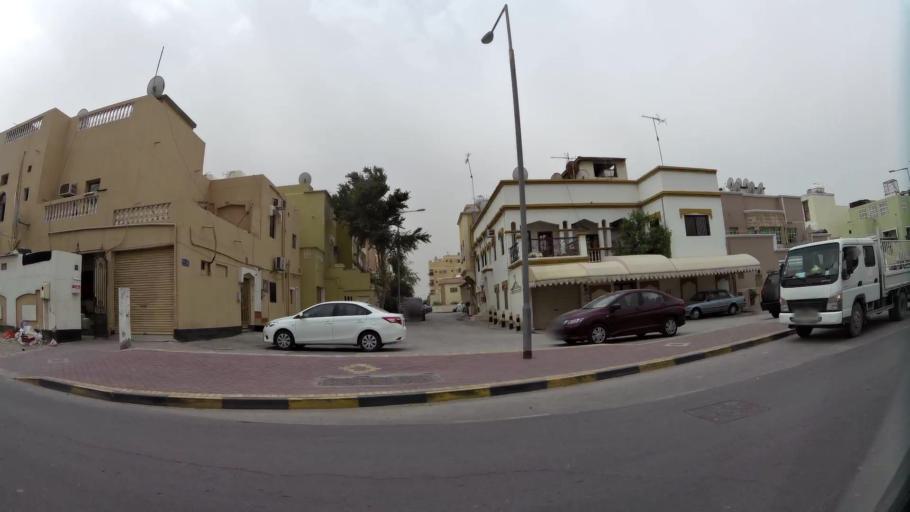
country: BH
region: Northern
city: Madinat `Isa
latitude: 26.1779
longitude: 50.5430
